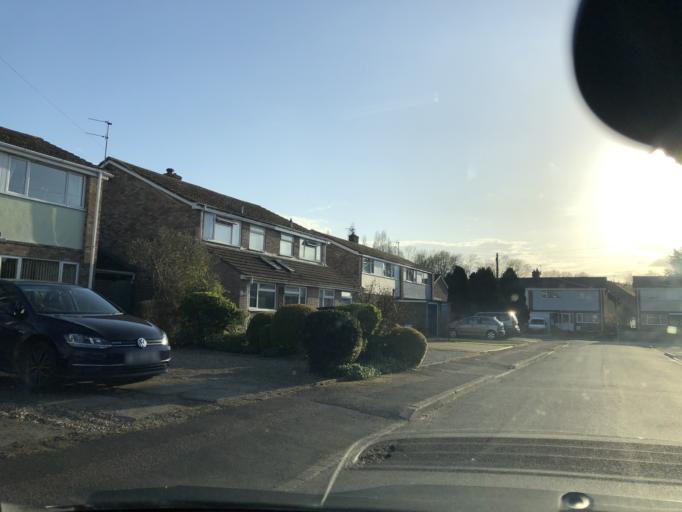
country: GB
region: England
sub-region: Oxfordshire
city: Witney
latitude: 51.7771
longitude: -1.4963
